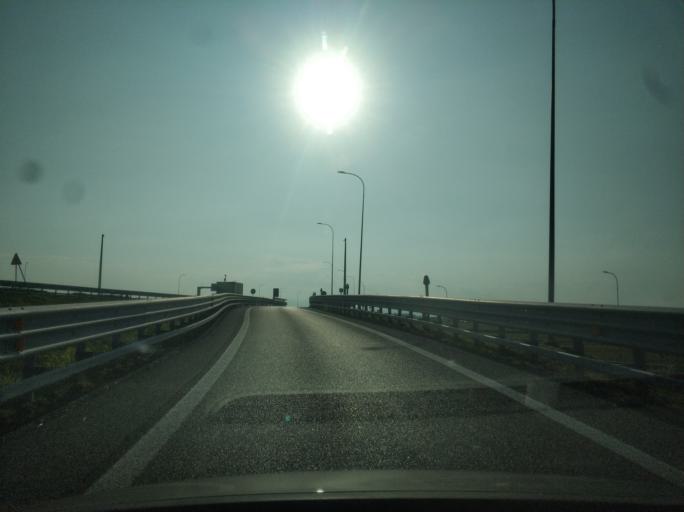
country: IT
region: Piedmont
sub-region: Provincia di Cuneo
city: Roreto
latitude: 44.6651
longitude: 7.8086
